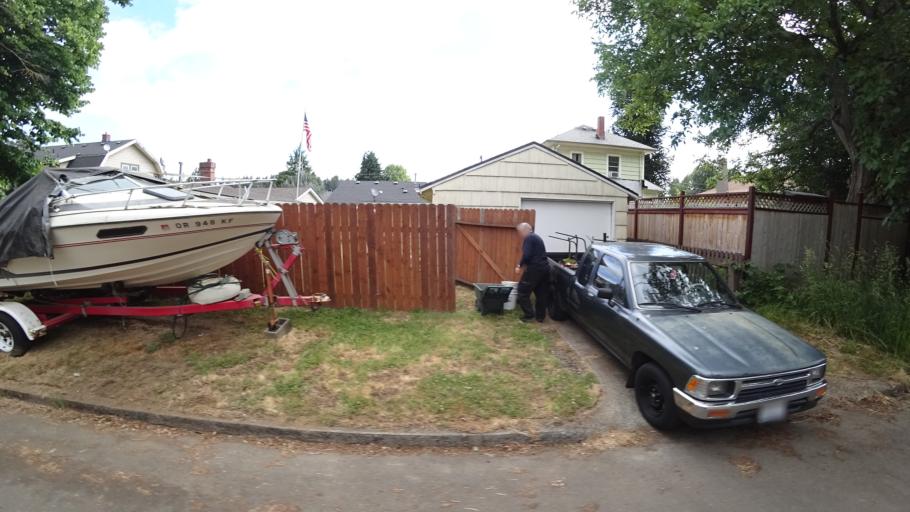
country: US
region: Oregon
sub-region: Washington County
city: West Haven
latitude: 45.5963
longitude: -122.7584
